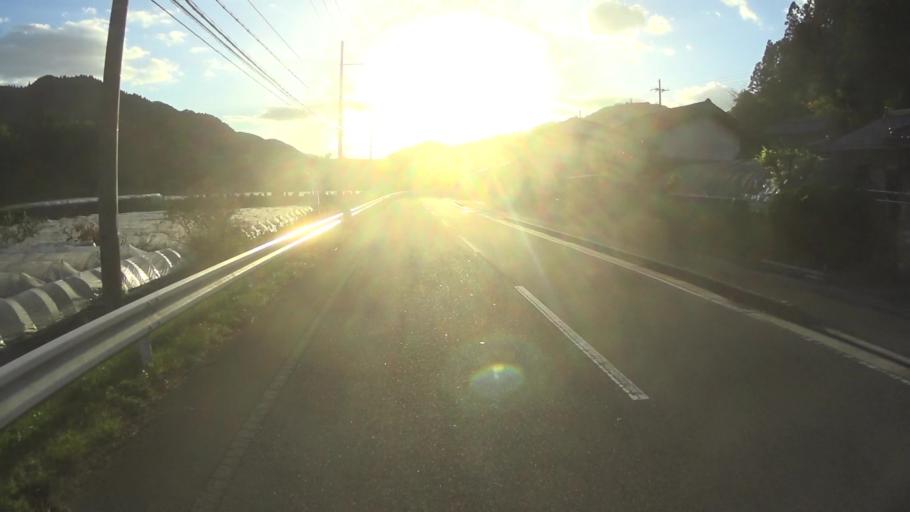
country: JP
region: Kyoto
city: Ayabe
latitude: 35.2319
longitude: 135.2520
